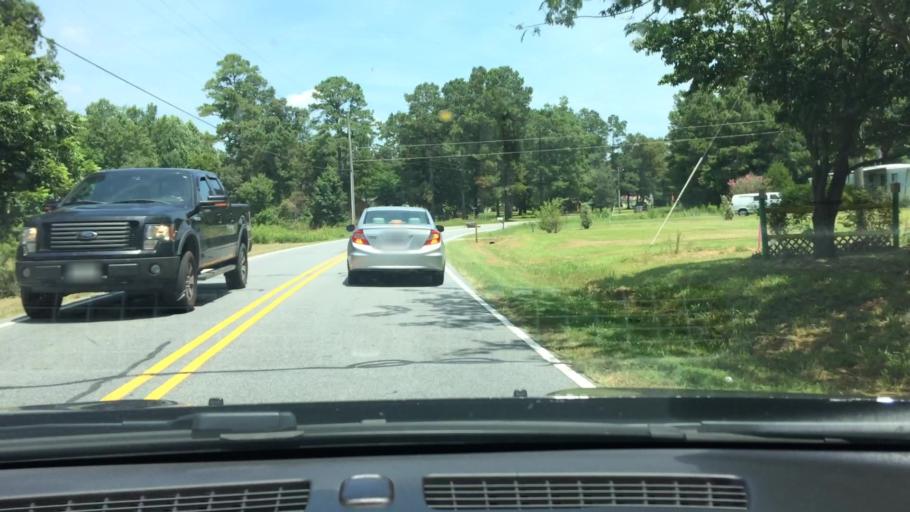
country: US
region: North Carolina
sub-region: Beaufort County
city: Washington
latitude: 35.5993
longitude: -77.1583
